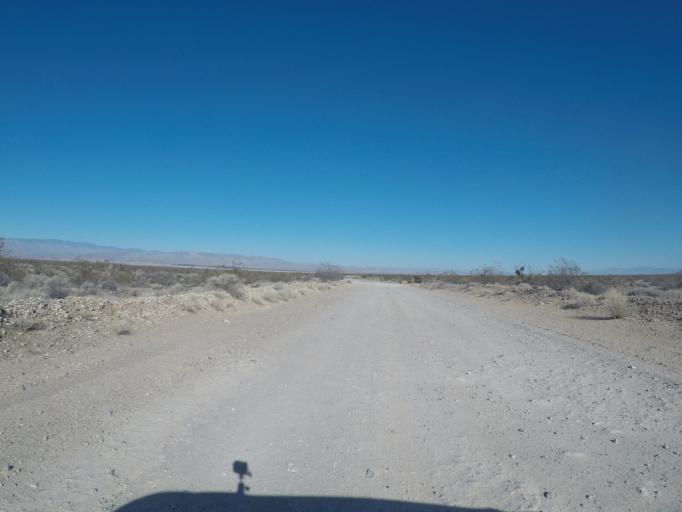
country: US
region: Nevada
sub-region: Clark County
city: Moapa Valley
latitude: 36.4461
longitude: -114.6766
